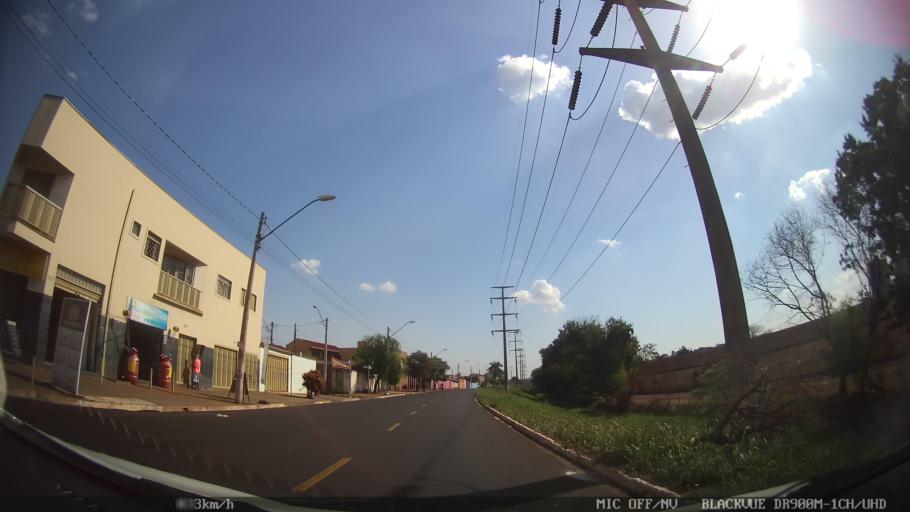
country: BR
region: Sao Paulo
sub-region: Ribeirao Preto
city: Ribeirao Preto
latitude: -21.1798
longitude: -47.8278
